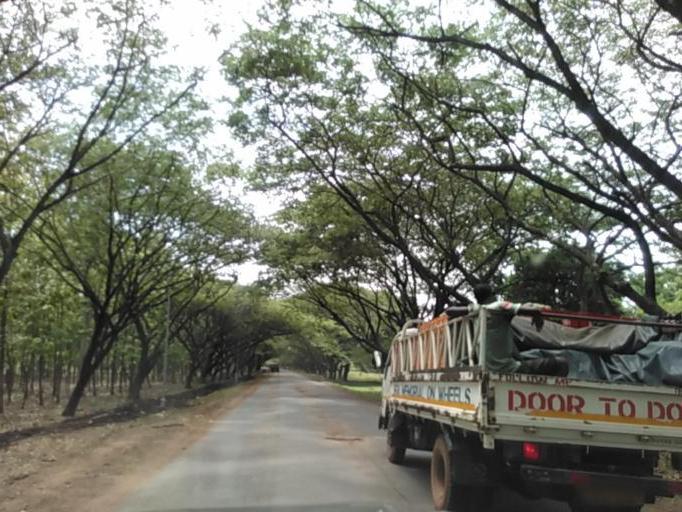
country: GH
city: Akropong
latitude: 6.0949
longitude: 0.1094
